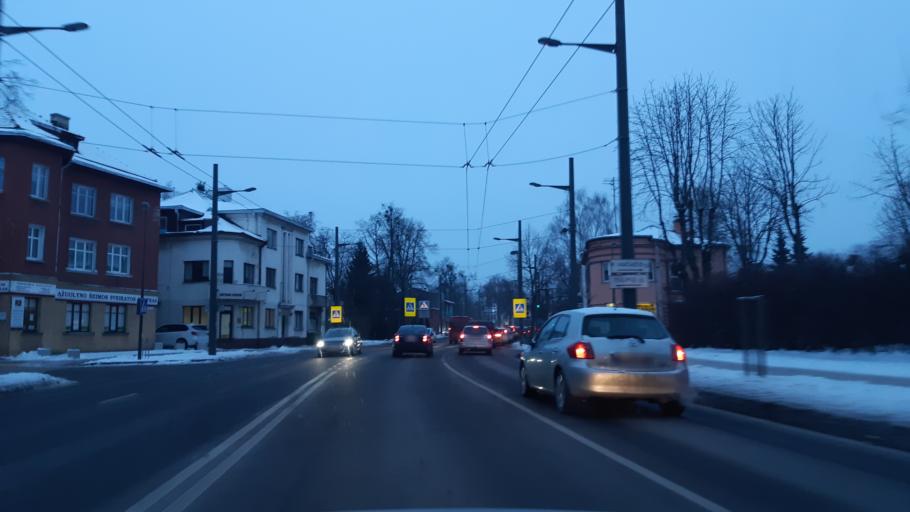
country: LT
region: Kauno apskritis
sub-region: Kaunas
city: Eiguliai
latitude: 54.9013
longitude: 23.9314
